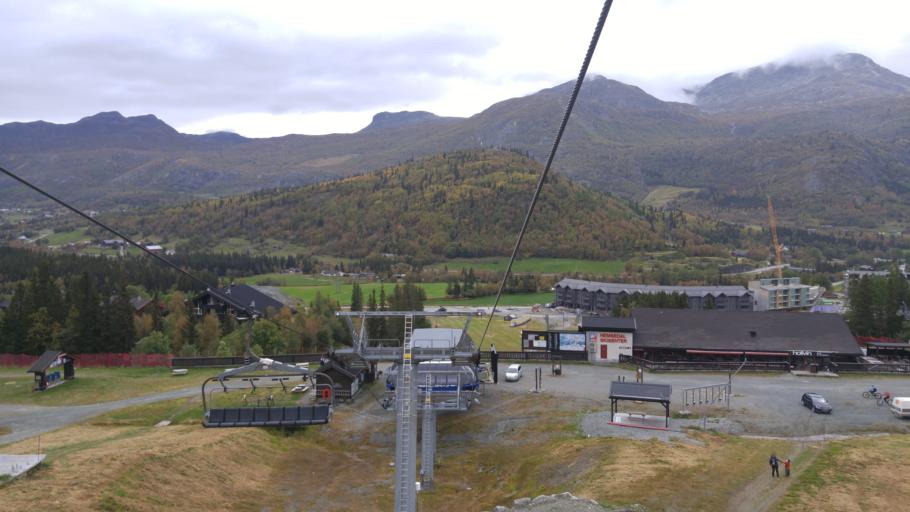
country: NO
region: Buskerud
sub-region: Hemsedal
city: Hemsedal
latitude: 60.8593
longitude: 8.5134
